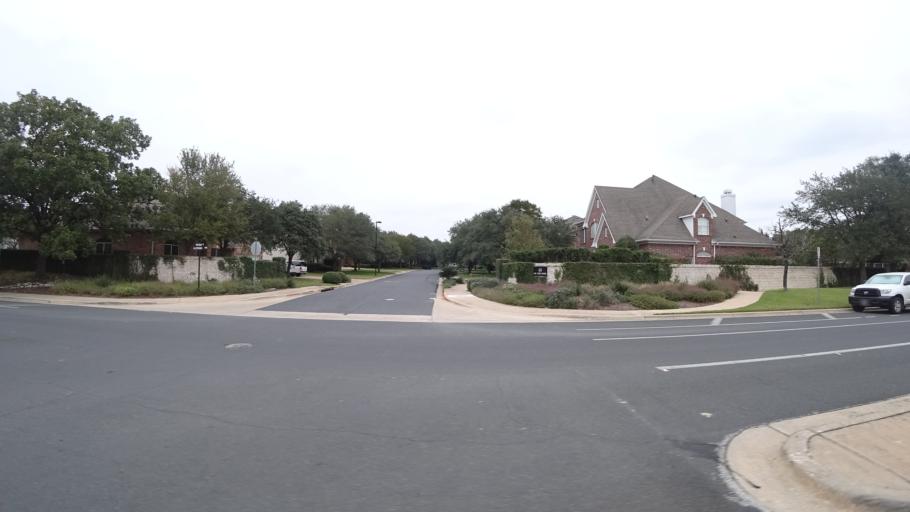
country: US
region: Texas
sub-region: Travis County
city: Shady Hollow
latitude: 30.1923
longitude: -97.8816
